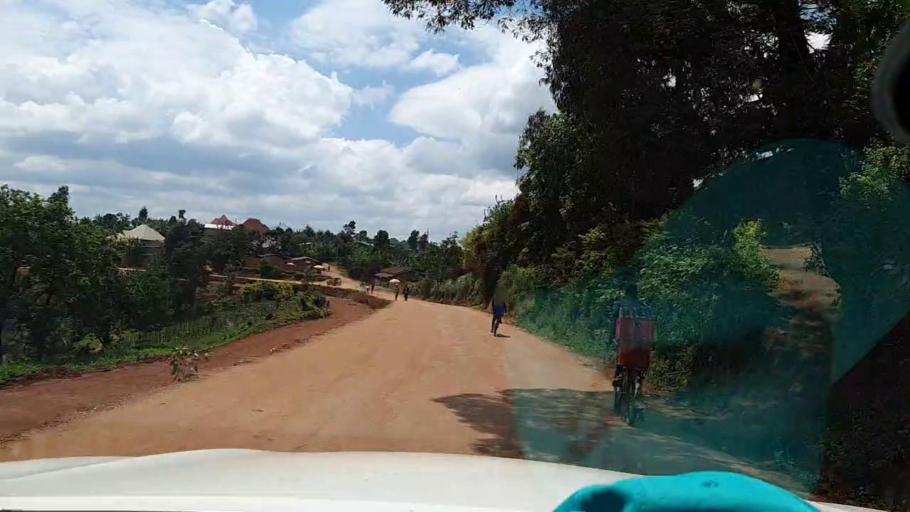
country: RW
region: Southern Province
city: Nzega
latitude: -2.6512
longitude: 29.5565
